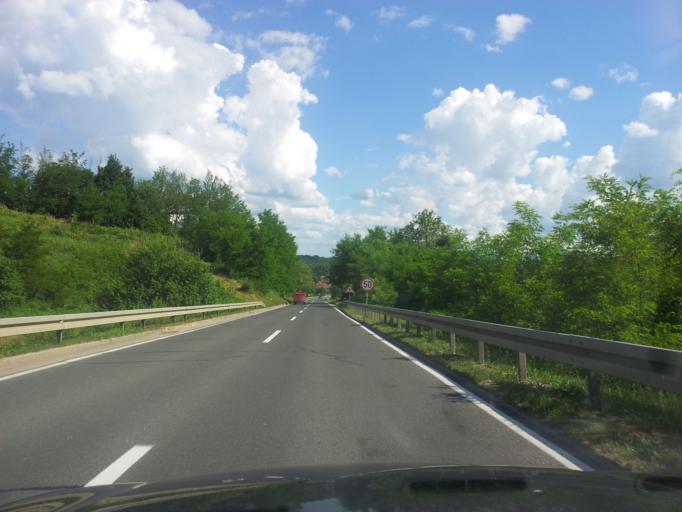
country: HR
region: Karlovacka
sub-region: Grad Karlovac
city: Karlovac
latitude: 45.4403
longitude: 15.4954
